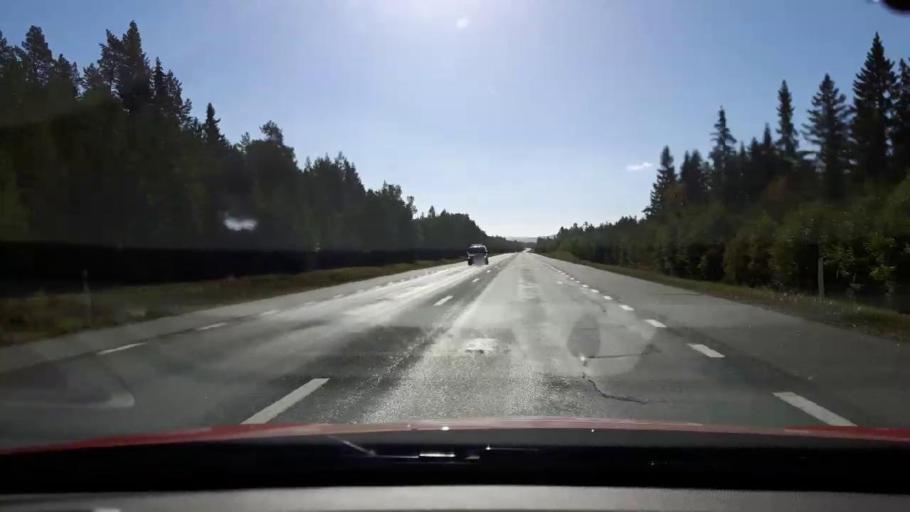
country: SE
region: Vaesternorrland
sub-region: Ange Kommun
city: Ange
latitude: 62.5871
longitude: 15.7212
